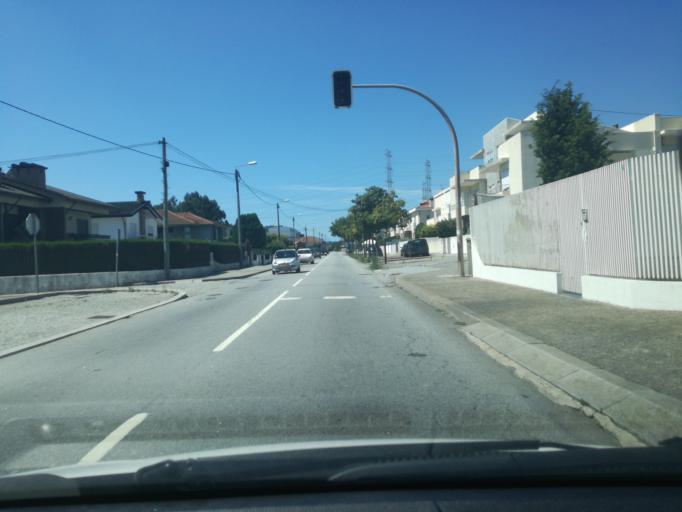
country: PT
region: Porto
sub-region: Maia
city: Nogueira
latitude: 41.2317
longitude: -8.5910
